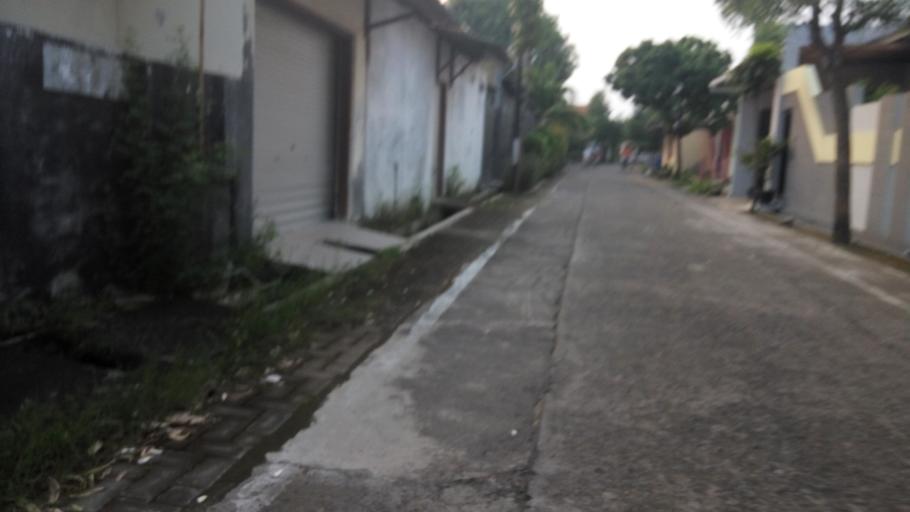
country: ID
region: Central Java
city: Semarang
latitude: -6.9876
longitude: 110.4066
